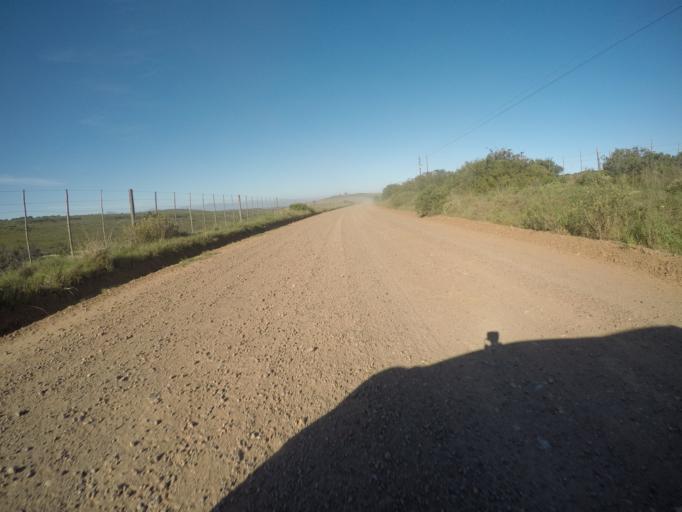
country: ZA
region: Western Cape
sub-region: Eden District Municipality
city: Mossel Bay
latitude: -34.1445
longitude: 22.0040
